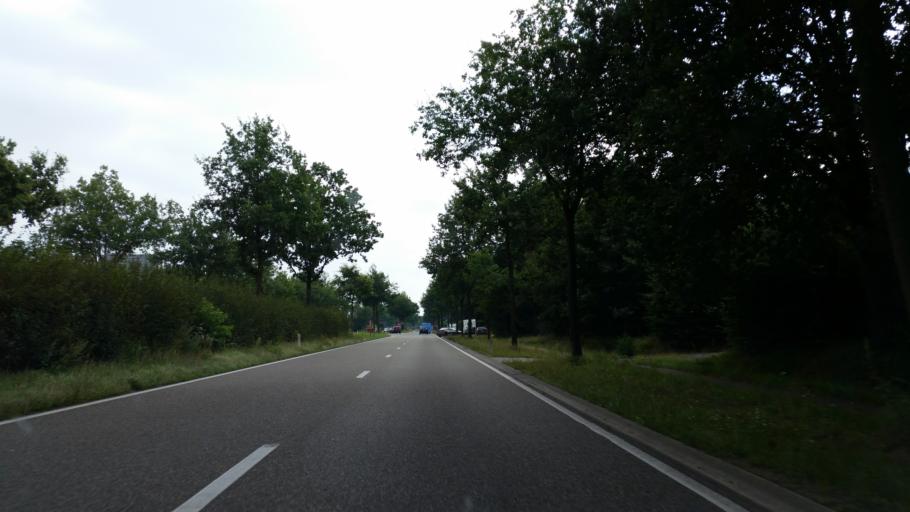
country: BE
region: Flanders
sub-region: Provincie Antwerpen
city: Kasterlee
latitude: 51.2777
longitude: 4.9545
